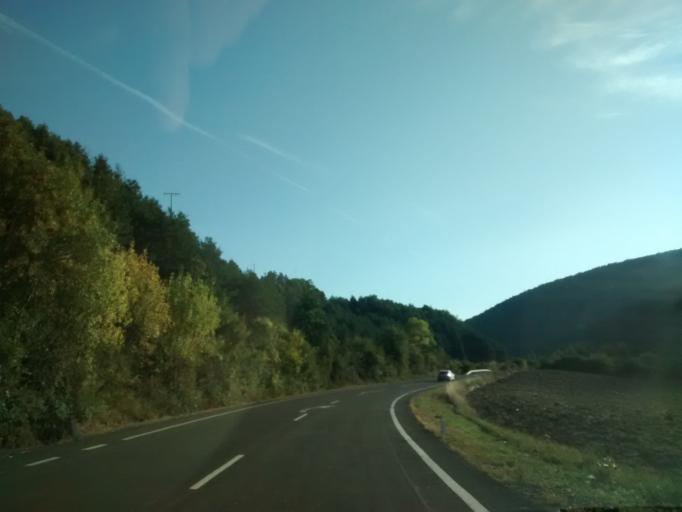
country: ES
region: Aragon
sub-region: Provincia de Huesca
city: Santa Cruz de la Seros
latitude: 42.6105
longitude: -0.7245
